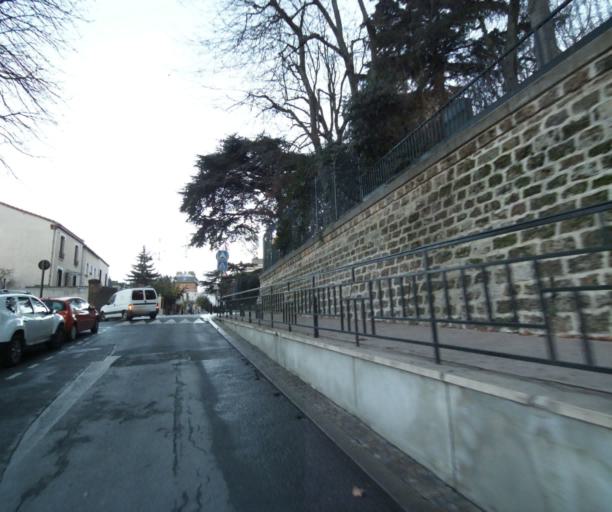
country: FR
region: Ile-de-France
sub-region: Departement des Hauts-de-Seine
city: Puteaux
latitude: 48.8835
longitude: 2.2328
